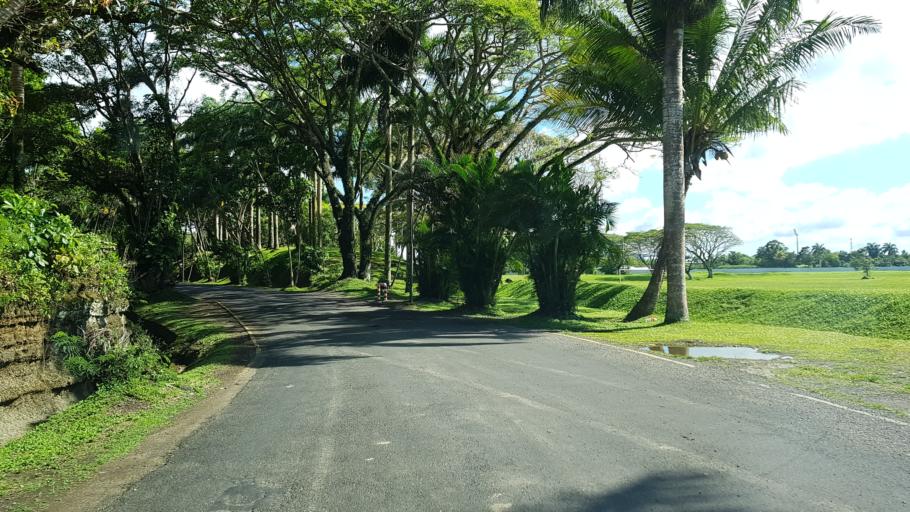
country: FJ
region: Central
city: Suva
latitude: -18.1553
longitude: 178.4440
